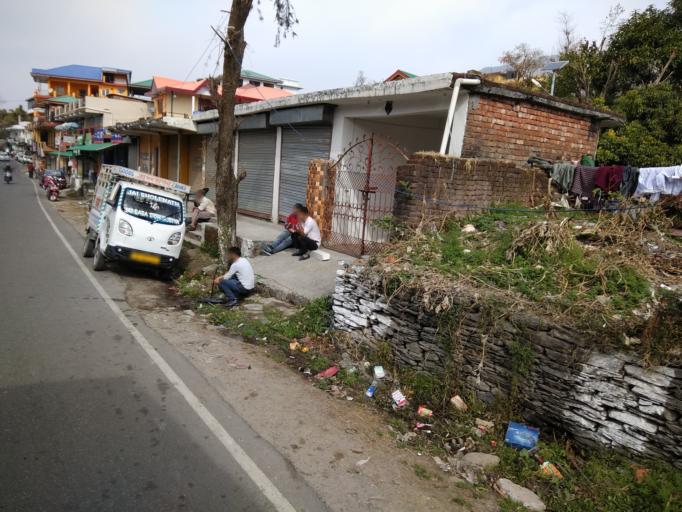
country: IN
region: Himachal Pradesh
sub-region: Kangra
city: Dharmsala
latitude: 32.1849
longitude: 76.3685
